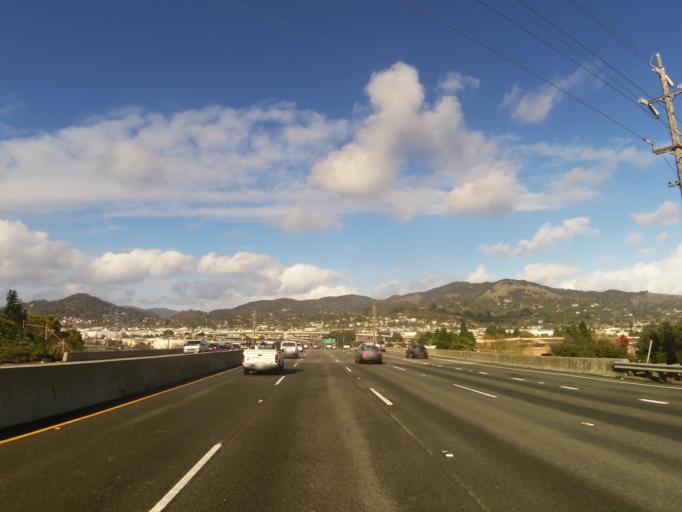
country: US
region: California
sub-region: Marin County
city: San Rafael
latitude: 37.9565
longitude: -122.5088
